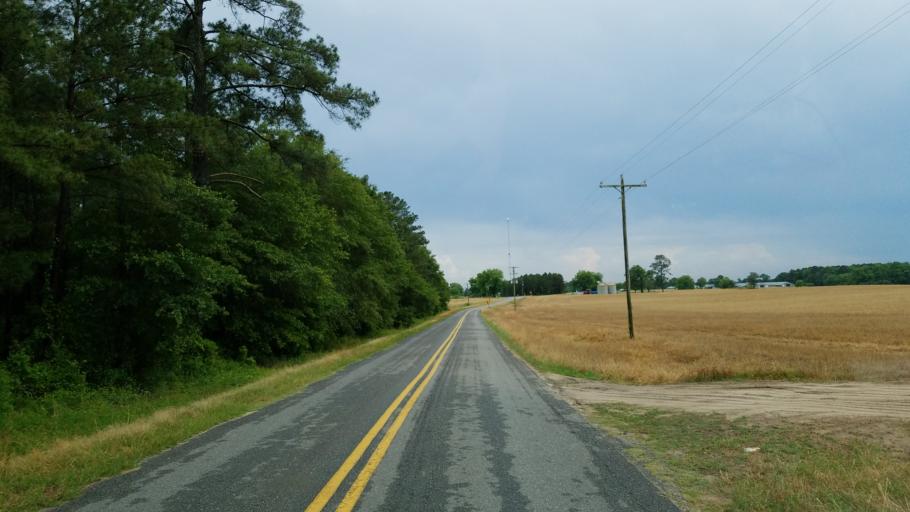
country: US
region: Georgia
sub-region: Dooly County
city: Unadilla
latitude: 32.2504
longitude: -83.7973
